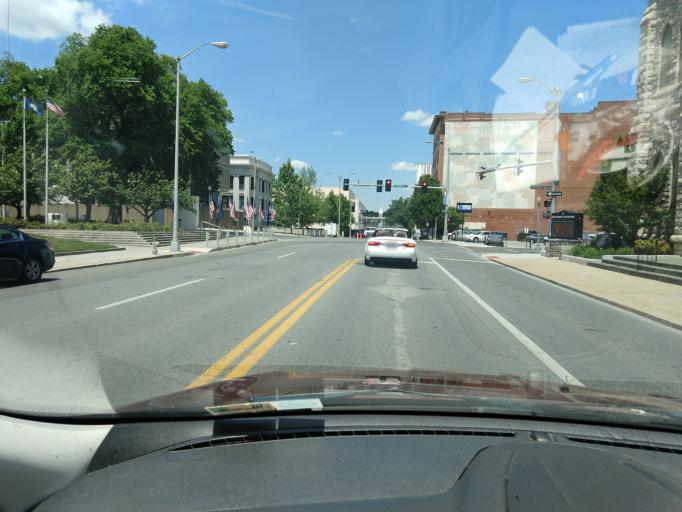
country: US
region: Virginia
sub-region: City of Roanoke
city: Roanoke
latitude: 37.2703
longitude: -79.9441
